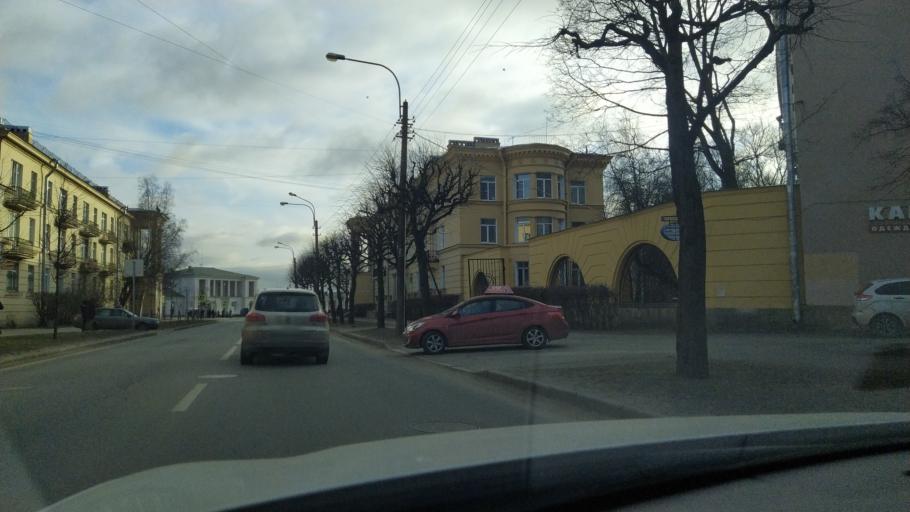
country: RU
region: St.-Petersburg
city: Pushkin
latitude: 59.7240
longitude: 30.4255
